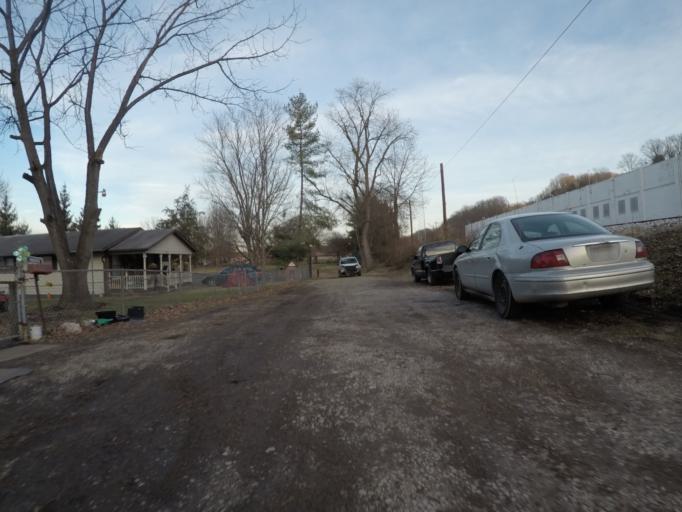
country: US
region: Ohio
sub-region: Lawrence County
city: Burlington
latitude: 38.3987
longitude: -82.5039
